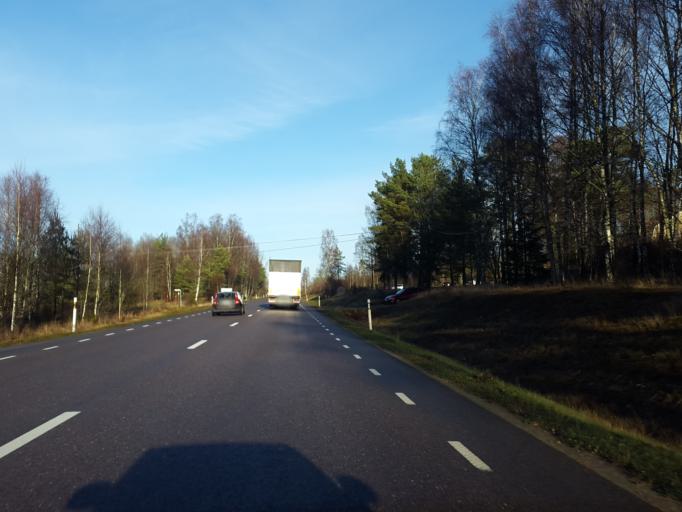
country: SE
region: Vaestra Goetaland
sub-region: Vargarda Kommun
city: Vargarda
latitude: 58.0069
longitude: 12.8157
